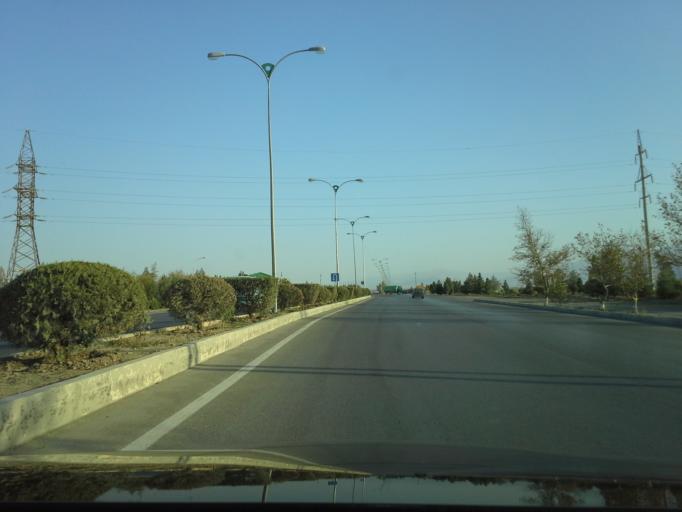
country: TM
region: Ahal
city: Abadan
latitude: 38.0249
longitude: 58.1999
